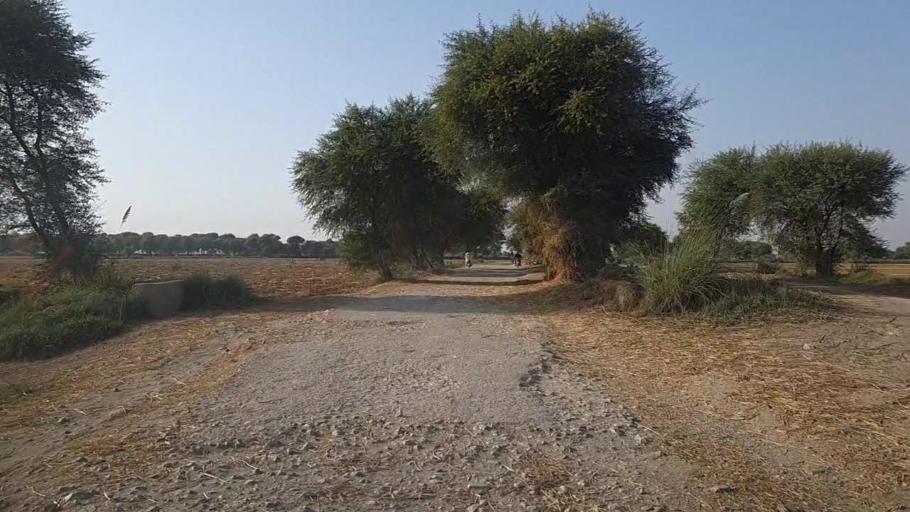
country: PK
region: Sindh
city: Kashmor
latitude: 28.4051
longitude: 69.4151
